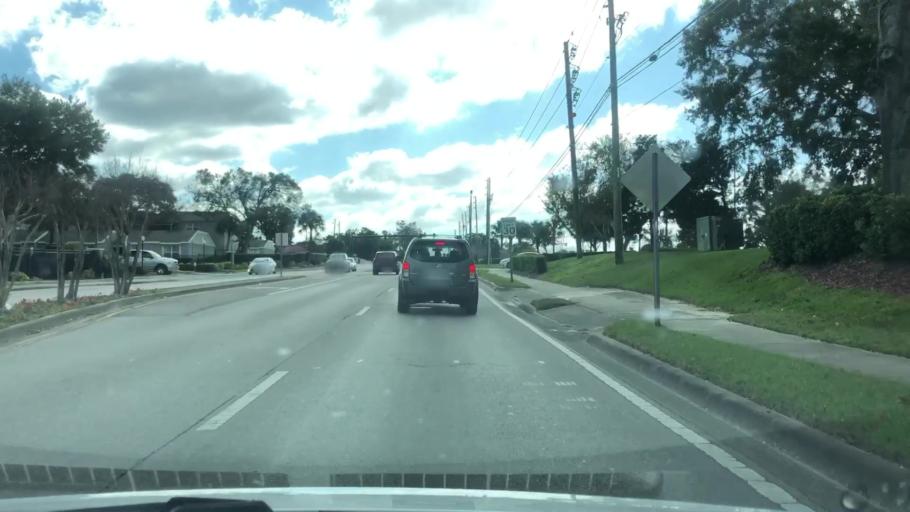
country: US
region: Florida
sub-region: Seminole County
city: Altamonte Springs
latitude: 28.6686
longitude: -81.3742
